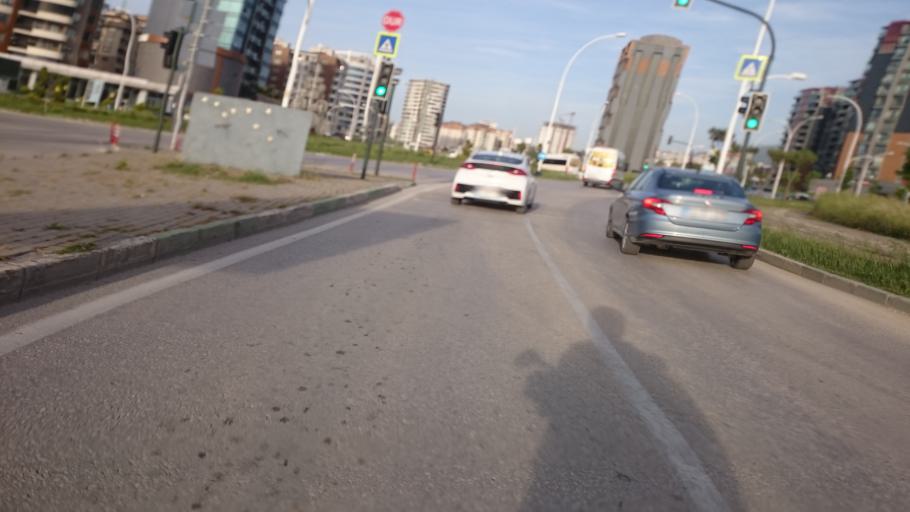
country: TR
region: Bursa
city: Cali
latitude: 40.2162
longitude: 28.9369
